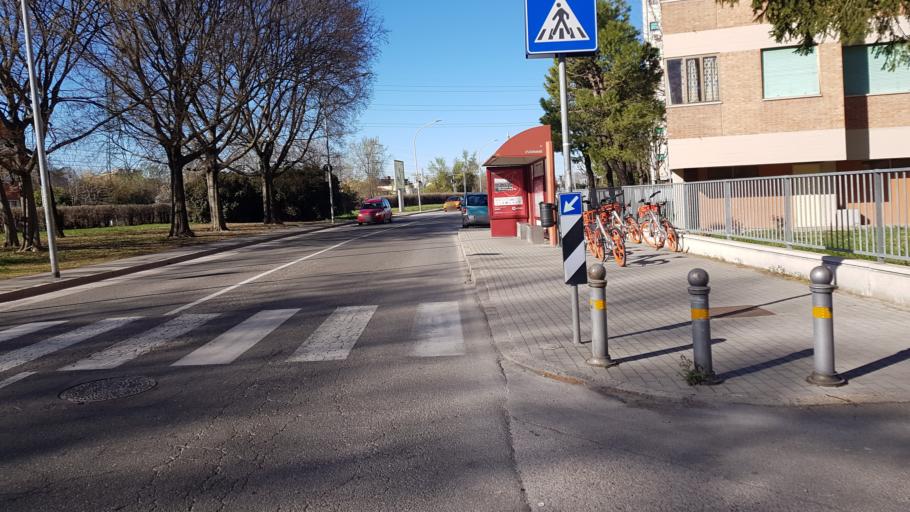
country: IT
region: Emilia-Romagna
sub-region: Provincia di Bologna
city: Bologna
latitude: 44.5185
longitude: 11.3245
